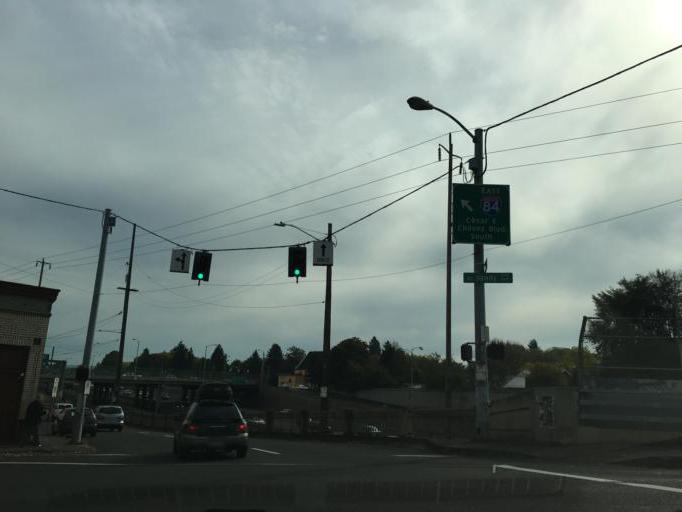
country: US
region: Oregon
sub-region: Multnomah County
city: Portland
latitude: 45.5341
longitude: -122.6249
